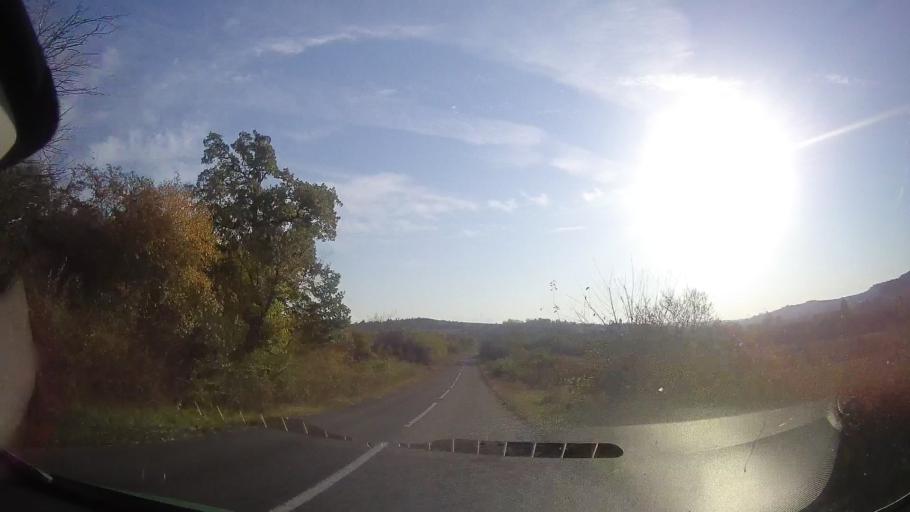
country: RO
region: Timis
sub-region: Comuna Bogda
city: Bogda
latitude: 45.9811
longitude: 21.5663
